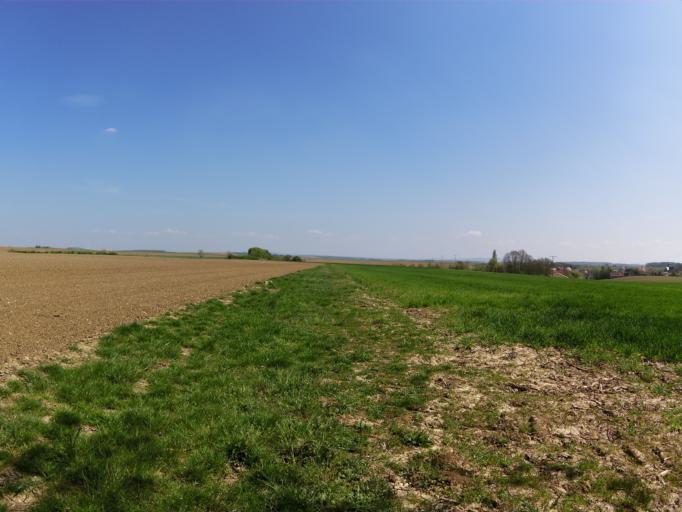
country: DE
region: Bavaria
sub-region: Regierungsbezirk Unterfranken
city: Giebelstadt
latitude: 49.6765
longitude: 9.9482
